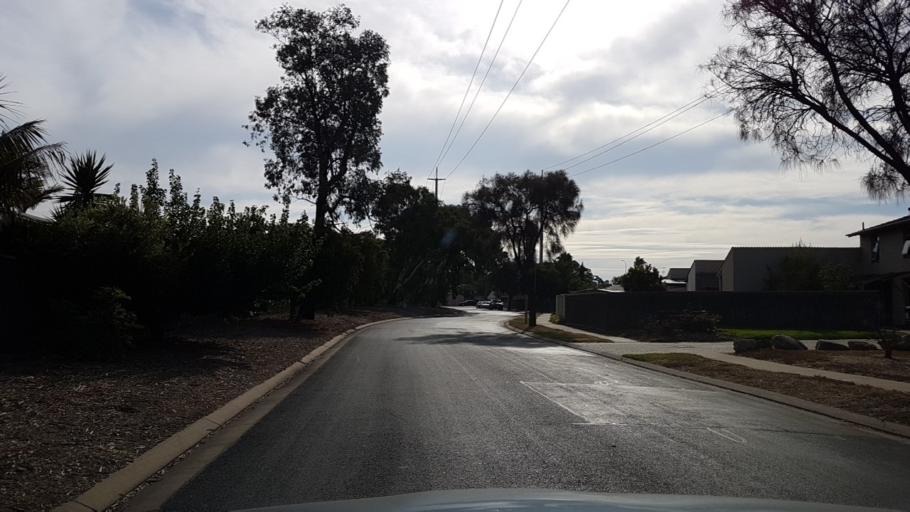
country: AU
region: South Australia
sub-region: Charles Sturt
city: West Lakes Shore
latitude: -34.8579
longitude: 138.4960
